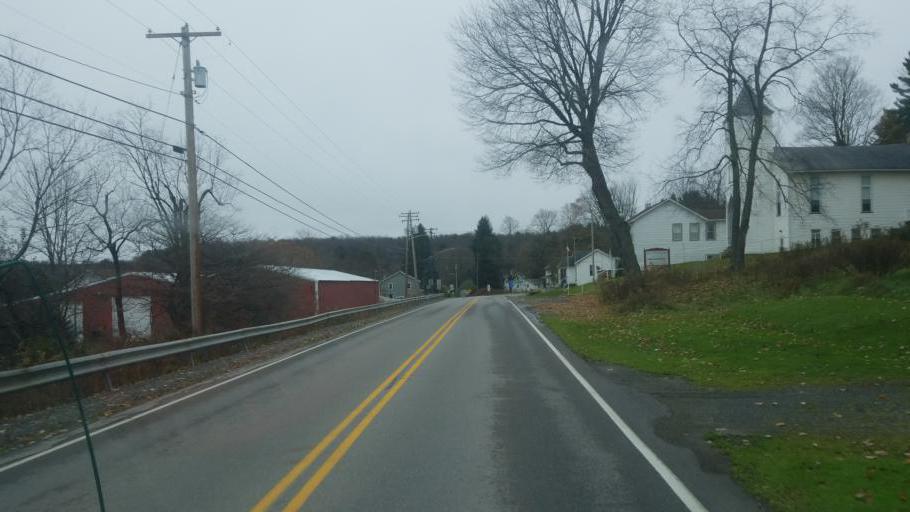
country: US
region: Pennsylvania
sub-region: Elk County
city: Saint Marys
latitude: 41.3541
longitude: -78.6082
